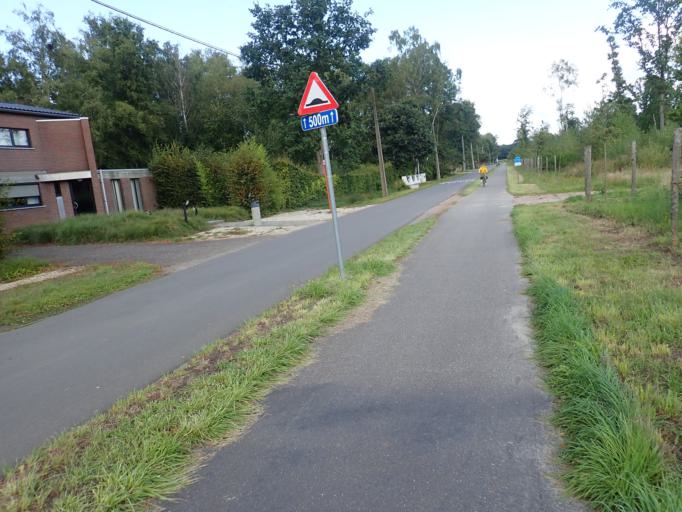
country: BE
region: Flanders
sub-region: Provincie Antwerpen
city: Zoersel
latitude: 51.2645
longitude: 4.6783
